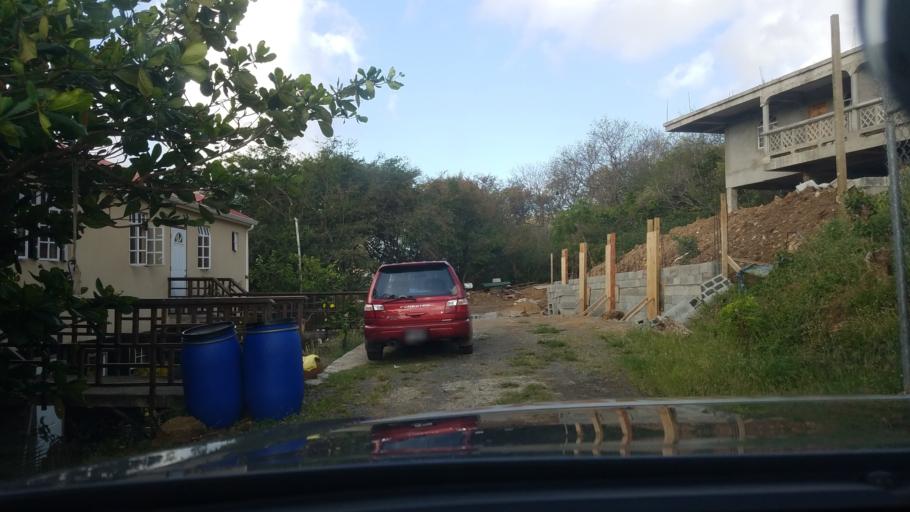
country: LC
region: Gros-Islet
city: Gros Islet
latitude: 14.0650
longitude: -60.9594
